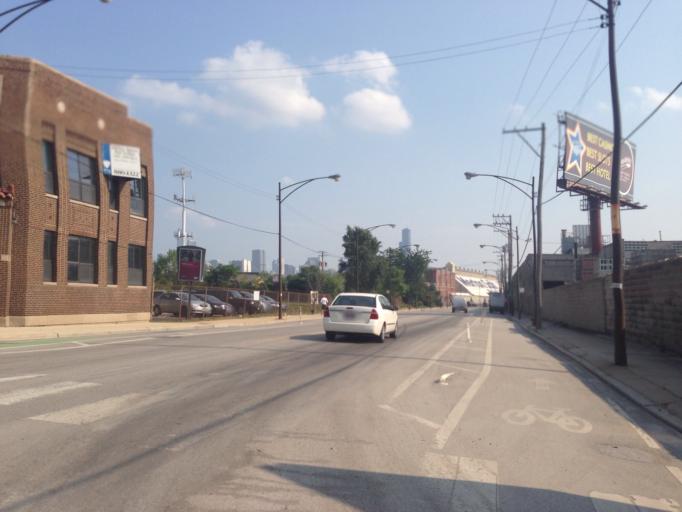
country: US
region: Illinois
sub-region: Cook County
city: Chicago
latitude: 41.9091
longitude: -87.6611
